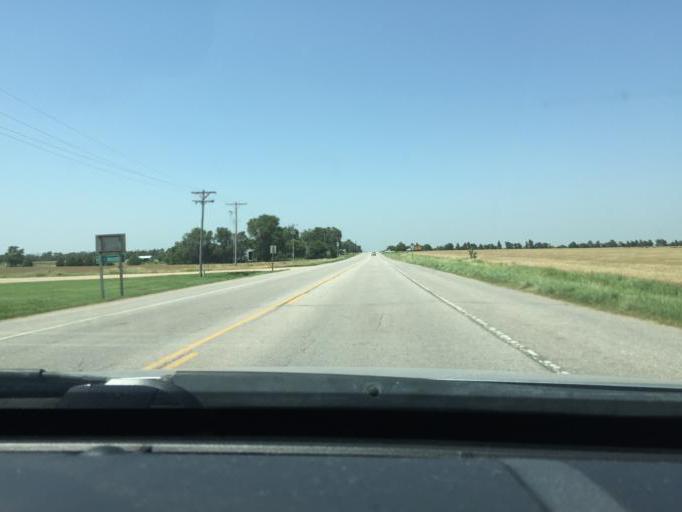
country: US
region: Kansas
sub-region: Reno County
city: Haven
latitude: 37.9417
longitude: -97.8667
